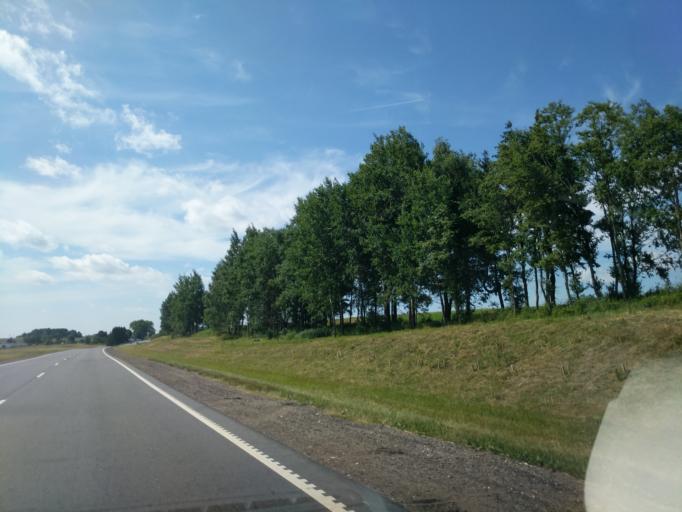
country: BY
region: Minsk
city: Syomkava
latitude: 54.0990
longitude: 27.4896
